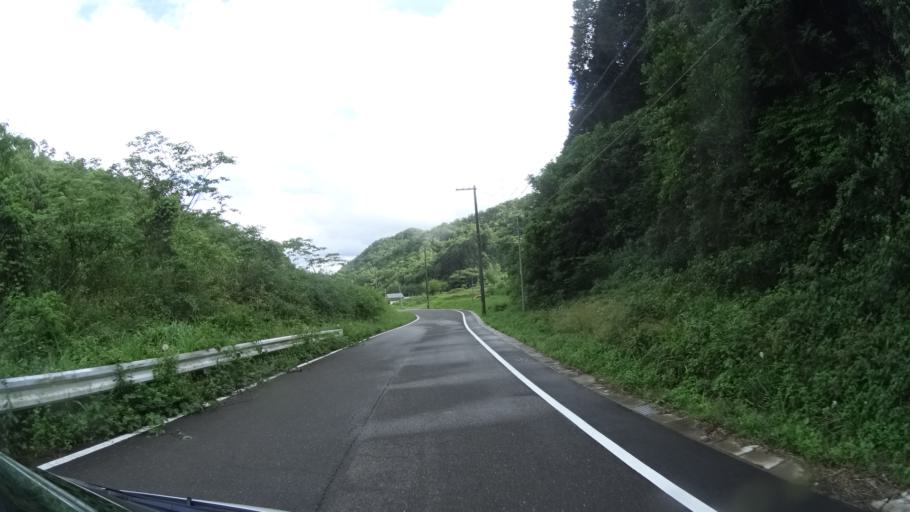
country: JP
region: Kyoto
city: Ayabe
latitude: 35.3669
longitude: 135.2887
